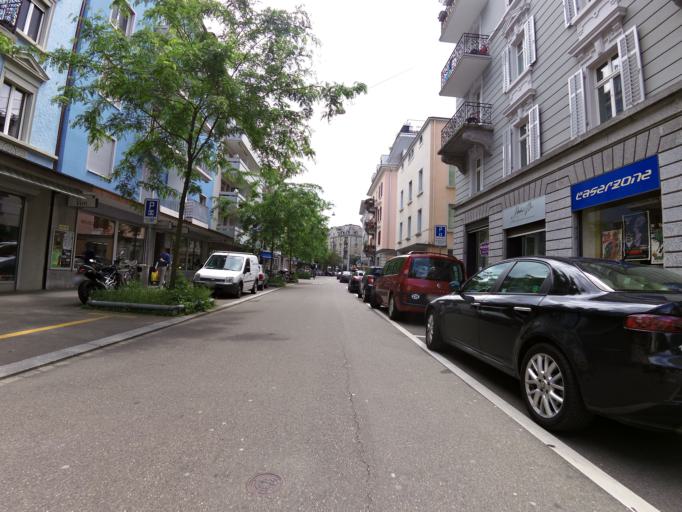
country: CH
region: Zurich
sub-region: Bezirk Zuerich
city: Zuerich (Kreis 4) / Langstrasse
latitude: 47.3746
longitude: 8.5292
